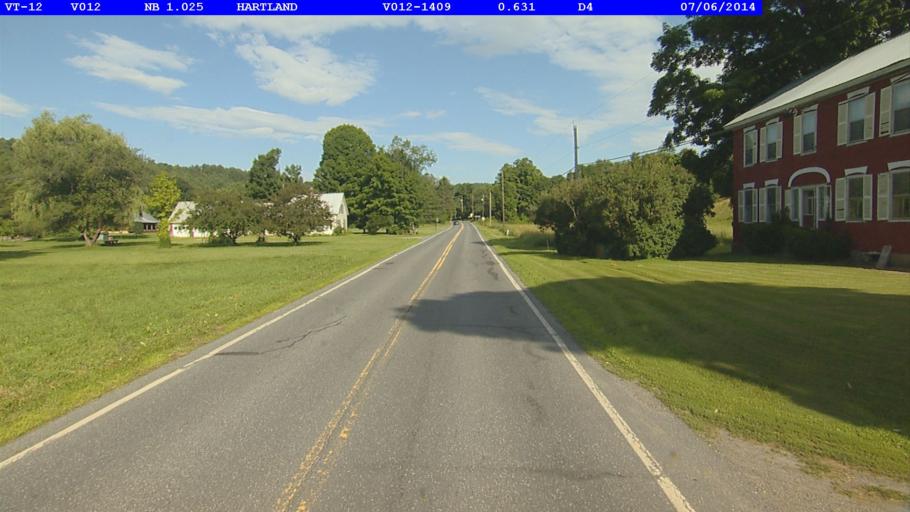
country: US
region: Vermont
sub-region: Windsor County
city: Windsor
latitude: 43.5454
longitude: -72.4093
